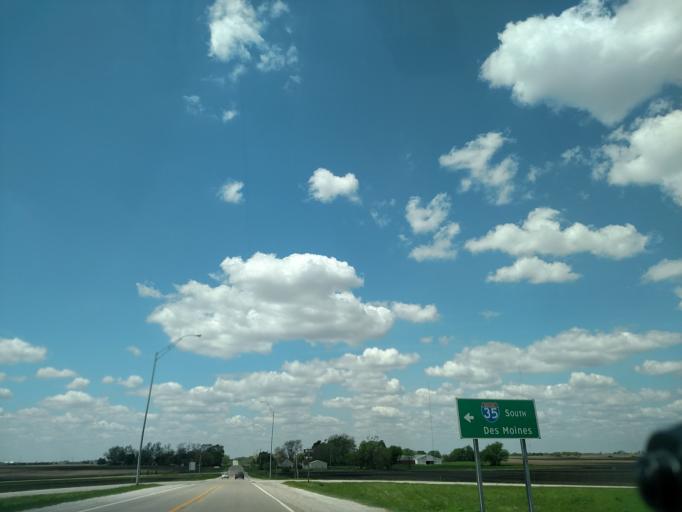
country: US
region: Iowa
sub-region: Polk County
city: Ankeny
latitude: 41.7914
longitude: -93.5712
